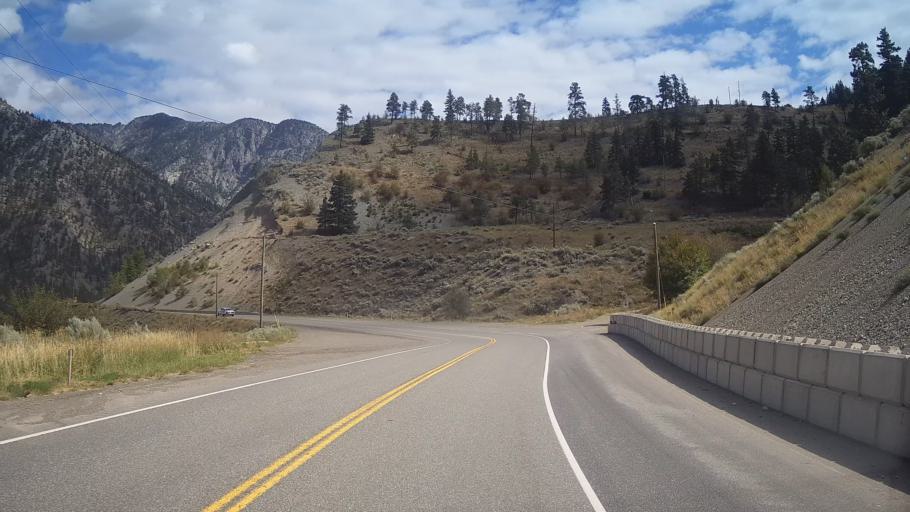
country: CA
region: British Columbia
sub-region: Thompson-Nicola Regional District
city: Ashcroft
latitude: 50.2516
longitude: -121.4748
